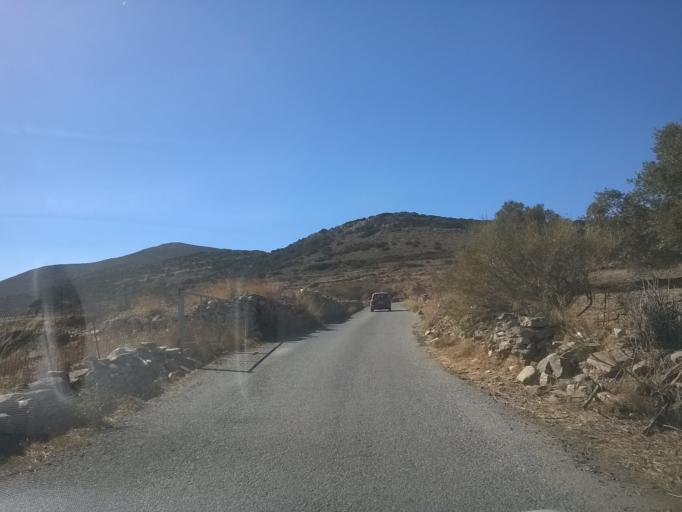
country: GR
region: South Aegean
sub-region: Nomos Kykladon
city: Filotion
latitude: 37.0273
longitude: 25.4281
